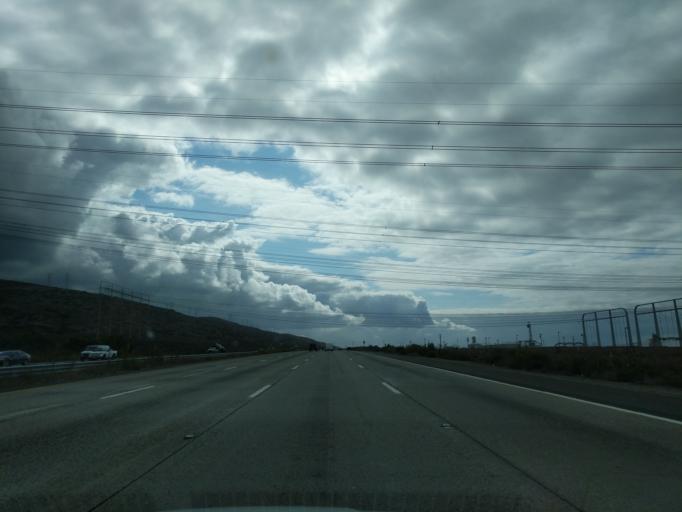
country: US
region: California
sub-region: Orange County
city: San Clemente
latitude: 33.3715
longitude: -117.5551
